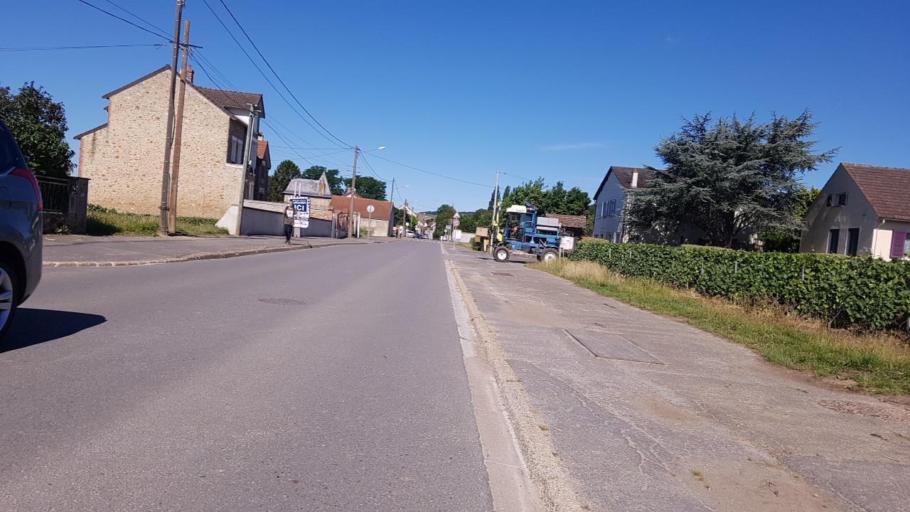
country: FR
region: Picardie
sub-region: Departement de l'Aisne
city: Charly-sur-Marne
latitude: 48.9765
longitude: 3.2953
